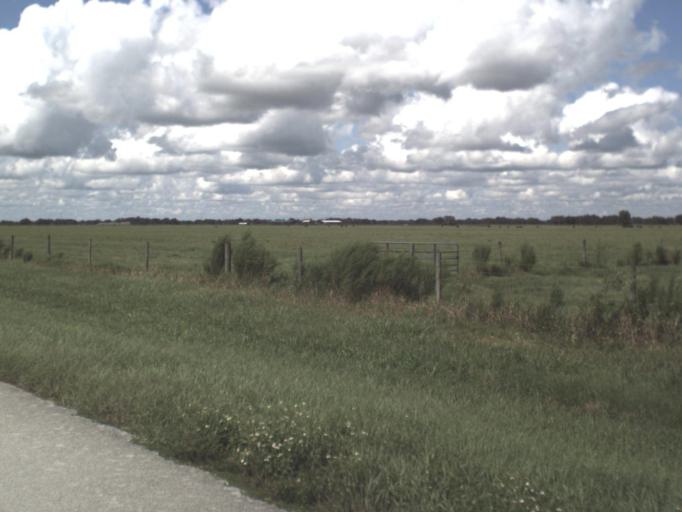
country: US
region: Florida
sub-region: DeSoto County
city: Arcadia
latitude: 27.2410
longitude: -81.9434
